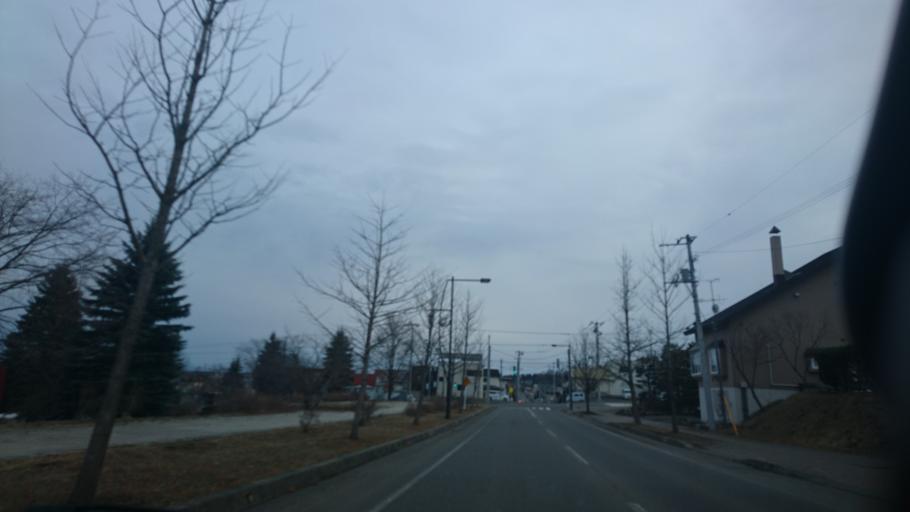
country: JP
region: Hokkaido
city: Otofuke
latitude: 42.9578
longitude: 143.2006
